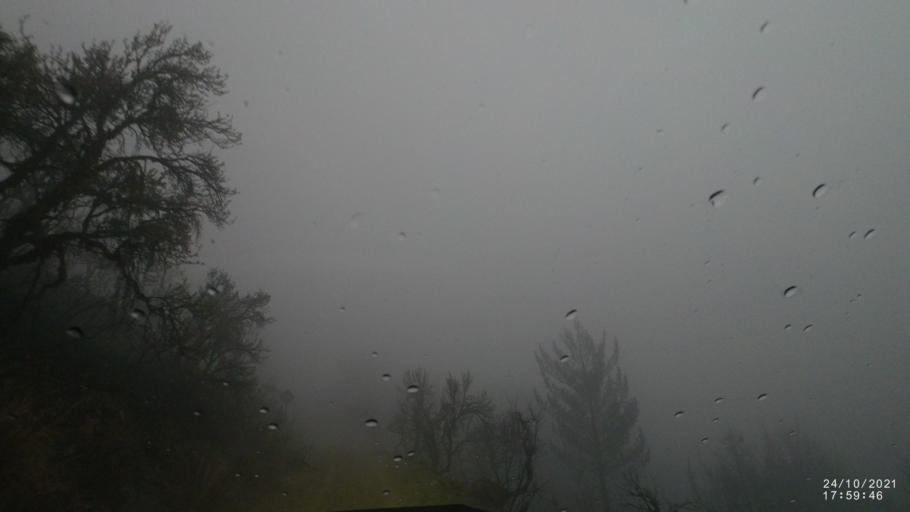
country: BO
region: Cochabamba
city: Cochabamba
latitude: -17.3255
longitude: -66.1316
